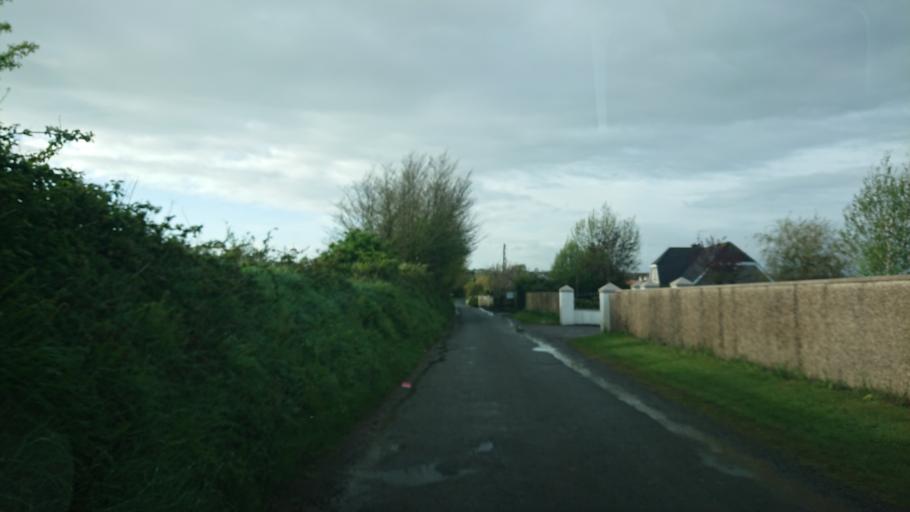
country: IE
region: Munster
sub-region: Waterford
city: Waterford
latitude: 52.2375
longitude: -7.1321
